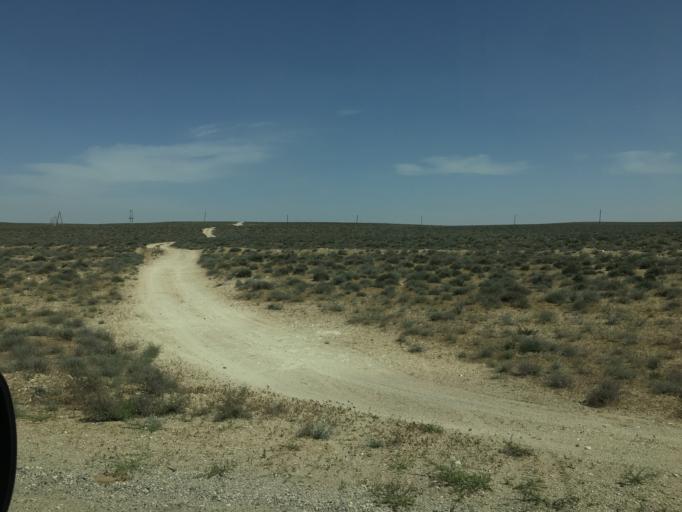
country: TM
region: Balkan
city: Balkanabat
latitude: 40.3154
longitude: 54.2337
